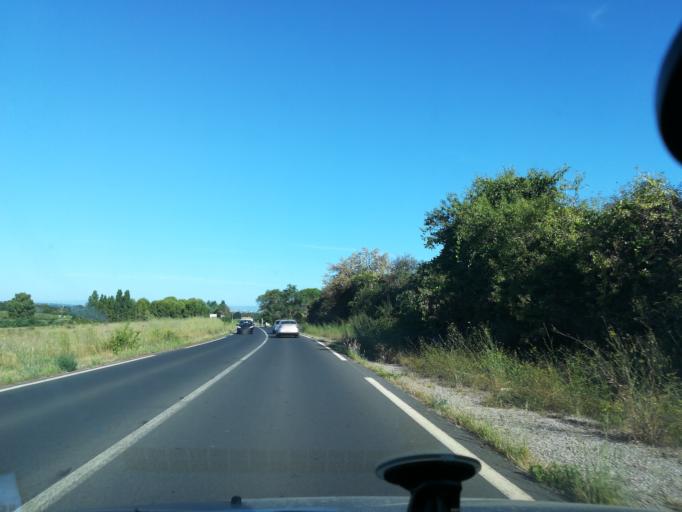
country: FR
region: Languedoc-Roussillon
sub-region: Departement de l'Herault
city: Portiragnes
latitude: 43.2987
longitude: 3.3413
